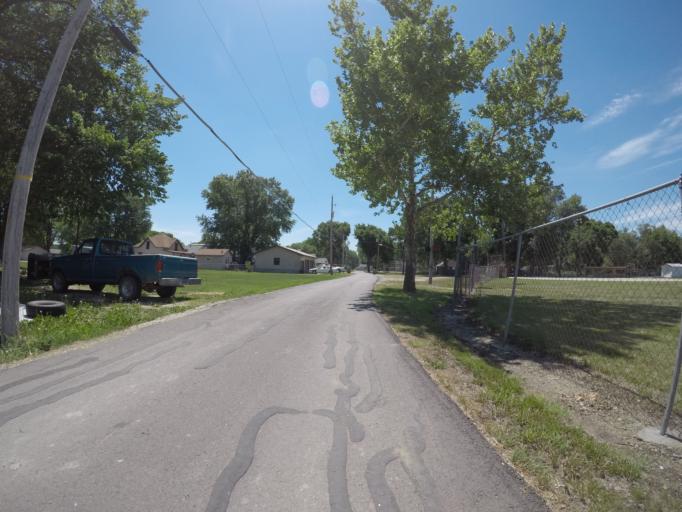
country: US
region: Kansas
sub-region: Wabaunsee County
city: Alma
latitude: 39.0548
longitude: -96.2400
